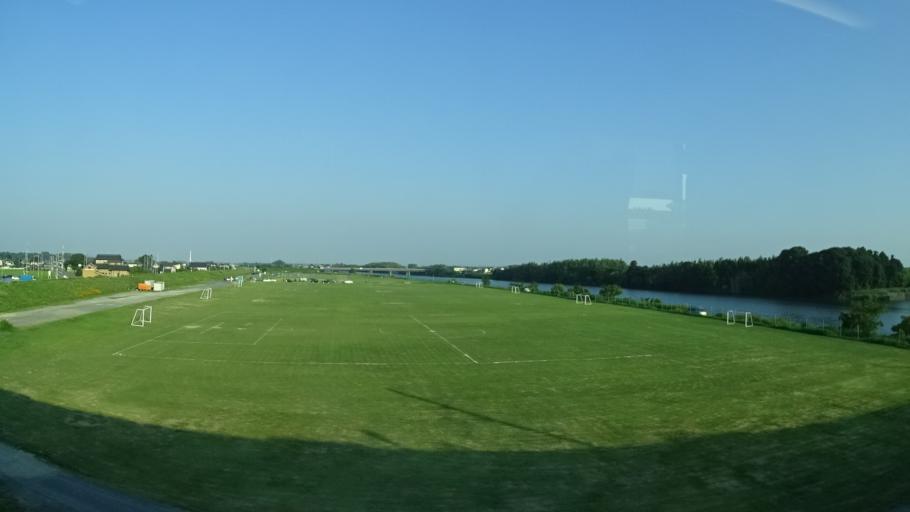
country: JP
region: Ibaraki
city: Katsuta
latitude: 36.3762
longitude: 140.5113
